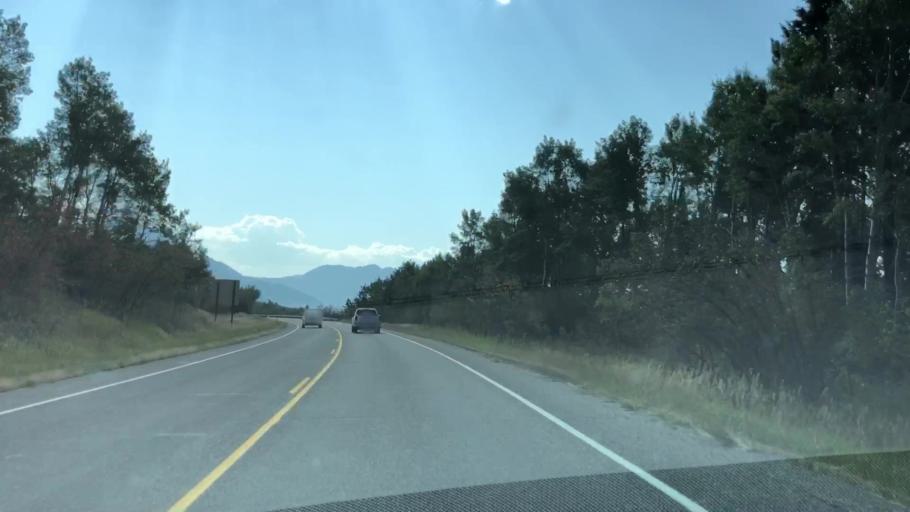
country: US
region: Wyoming
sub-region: Teton County
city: Hoback
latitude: 43.2095
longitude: -111.0578
